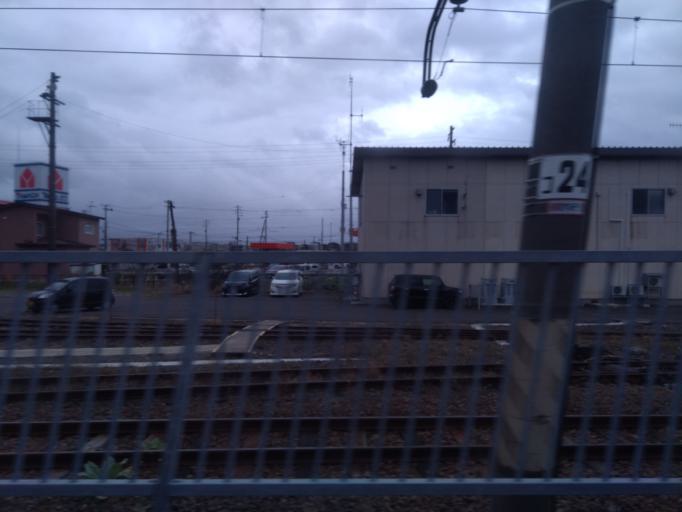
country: JP
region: Hokkaido
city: Hakodate
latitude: 41.8045
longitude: 140.7334
